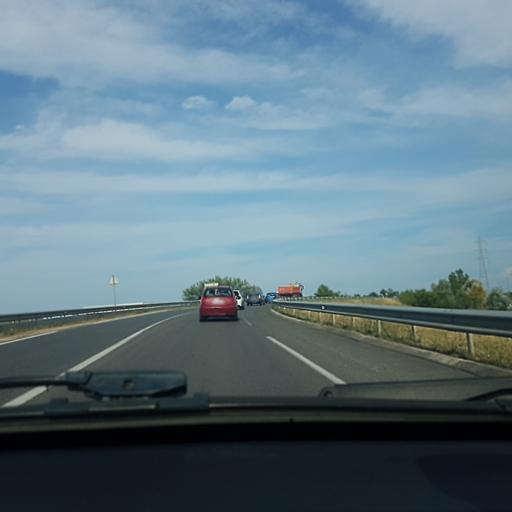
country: FR
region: Bourgogne
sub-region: Departement de Saone-et-Loire
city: Saint-Marcel
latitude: 46.7617
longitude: 4.8722
